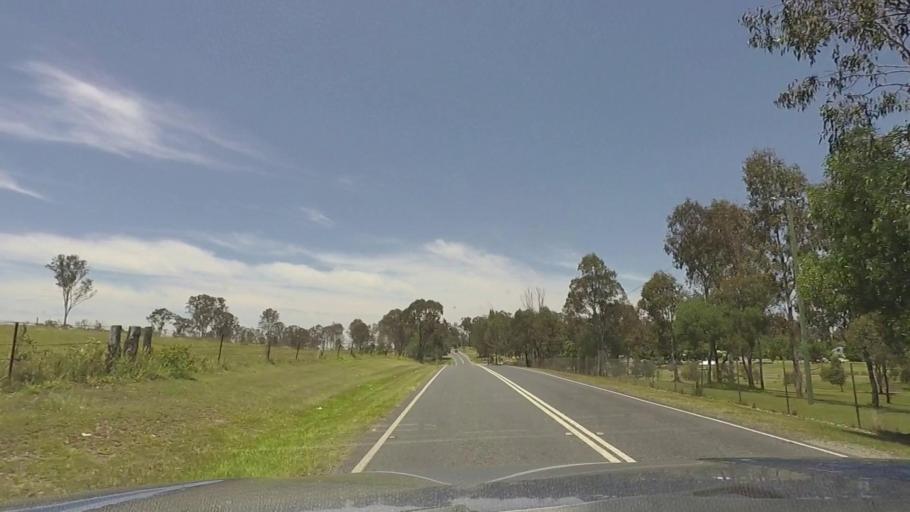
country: AU
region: Queensland
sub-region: Logan
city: North Maclean
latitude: -27.8239
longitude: 153.0266
